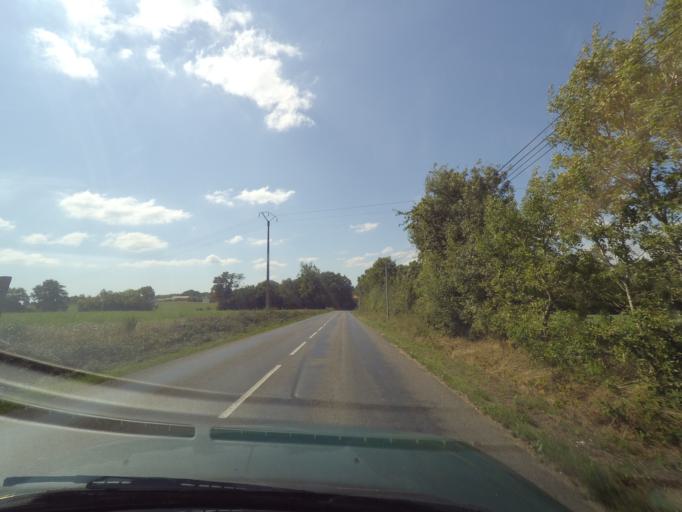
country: FR
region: Pays de la Loire
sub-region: Departement de la Loire-Atlantique
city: Saint-Lumine-de-Coutais
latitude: 47.0523
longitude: -1.7428
